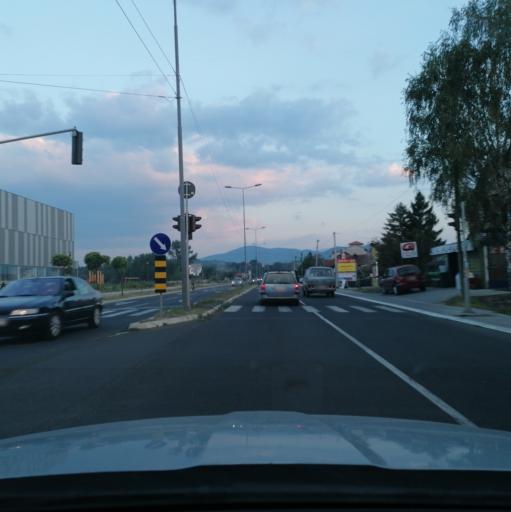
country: RS
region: Central Serbia
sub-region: Raski Okrug
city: Kraljevo
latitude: 43.7154
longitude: 20.6927
